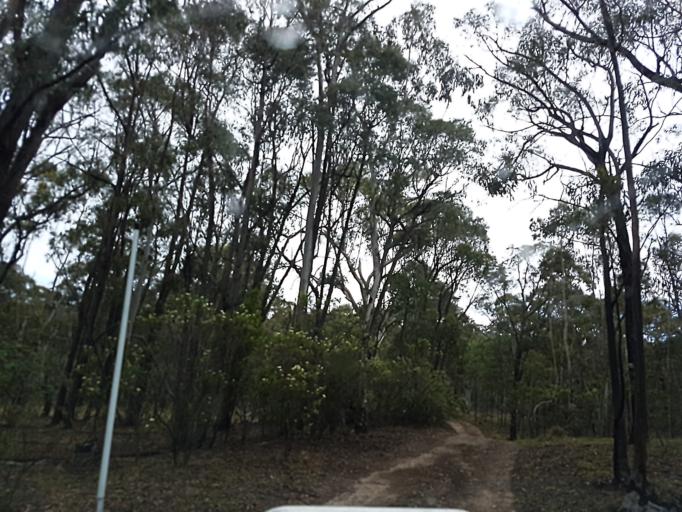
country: AU
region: New South Wales
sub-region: Snowy River
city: Jindabyne
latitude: -36.8815
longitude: 148.3388
